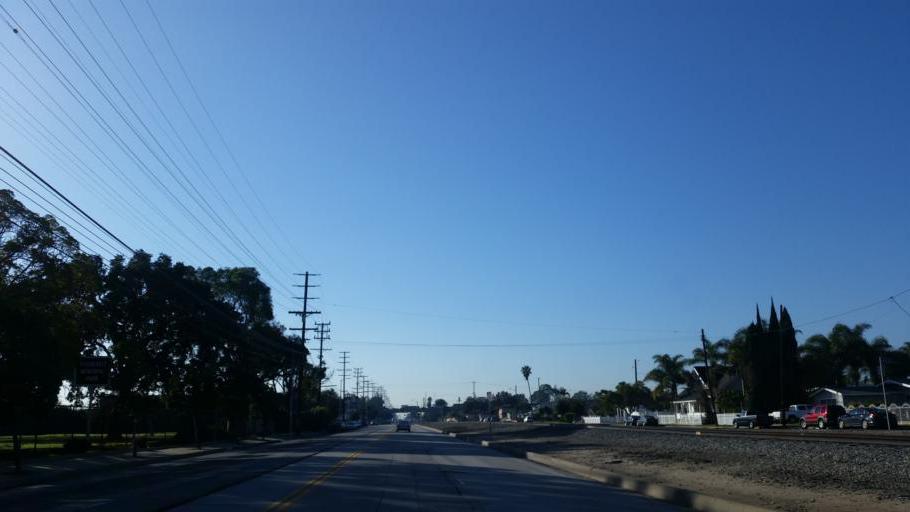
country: US
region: California
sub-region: Los Angeles County
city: Gardena
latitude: 33.8650
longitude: -118.2993
